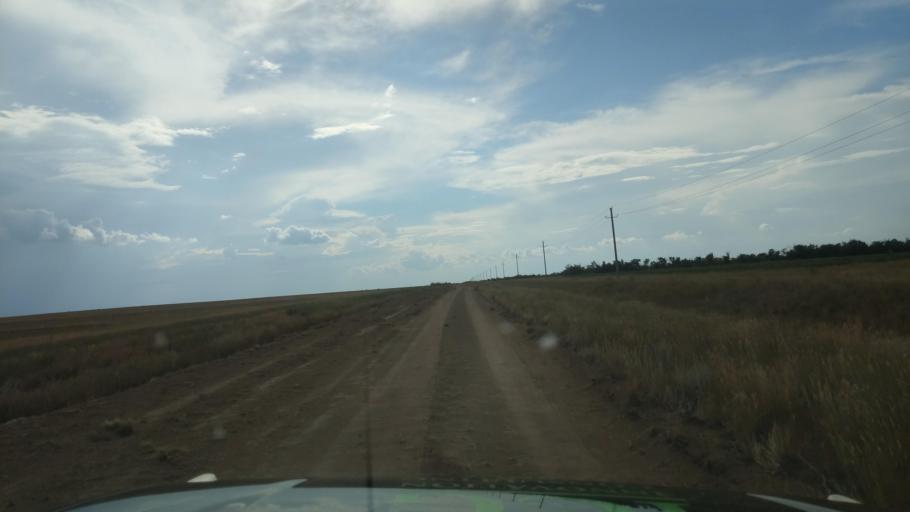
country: KZ
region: Pavlodar
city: Pavlodar
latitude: 52.5123
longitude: 77.5181
